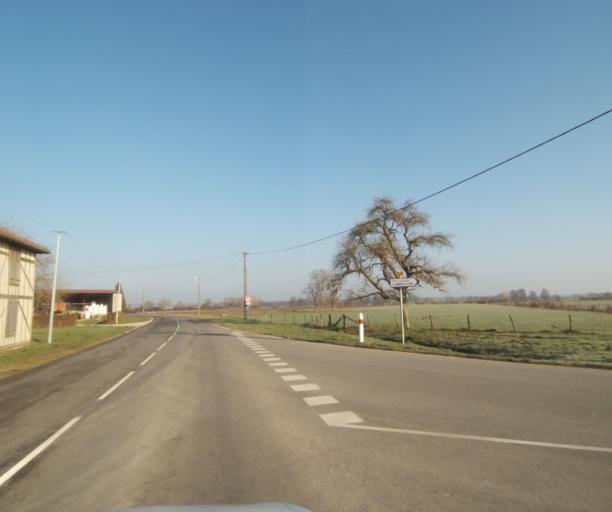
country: FR
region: Champagne-Ardenne
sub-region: Departement de la Haute-Marne
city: Montier-en-Der
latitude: 48.4569
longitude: 4.7693
